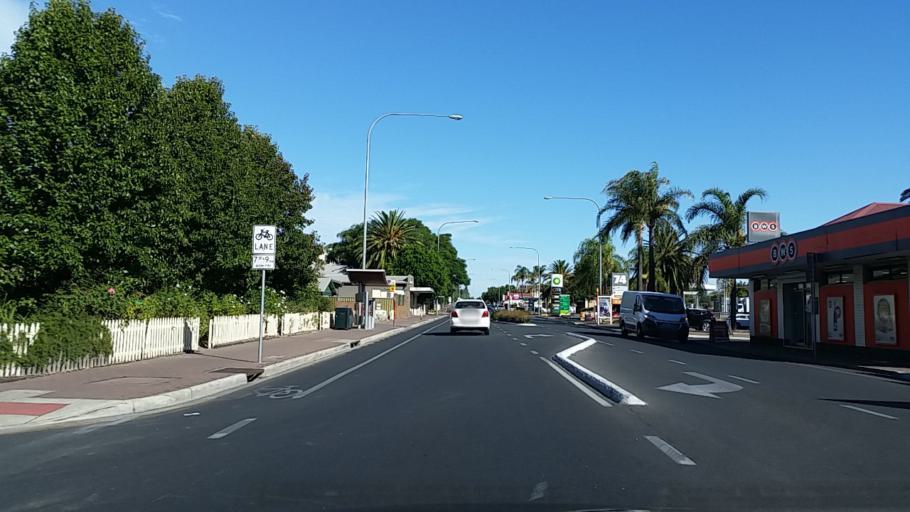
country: AU
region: South Australia
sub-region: Prospect
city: Prospect
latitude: -34.8899
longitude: 138.5942
